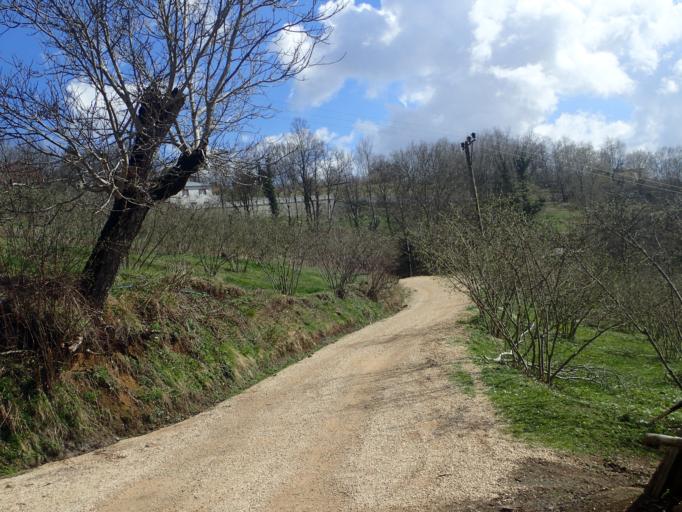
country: TR
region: Ordu
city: Kumru
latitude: 40.8040
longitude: 37.1855
